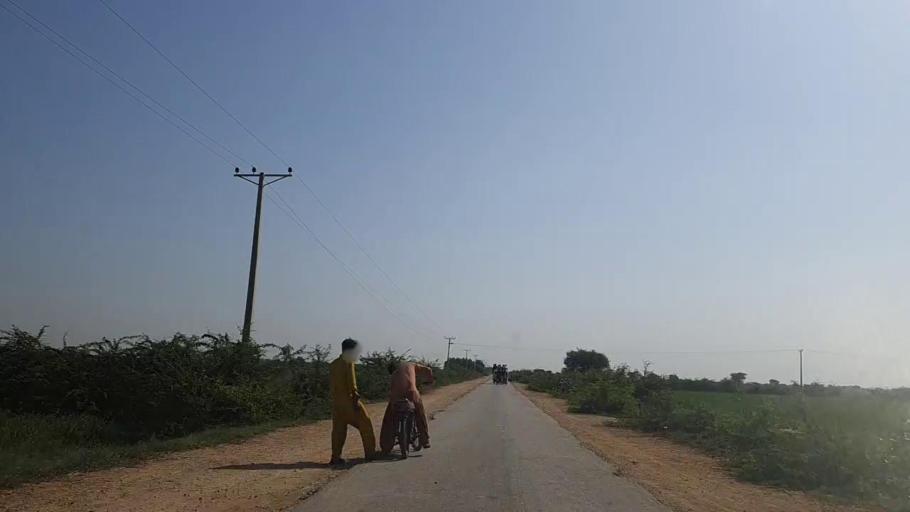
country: PK
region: Sindh
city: Mirpur Batoro
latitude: 24.6374
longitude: 68.2916
